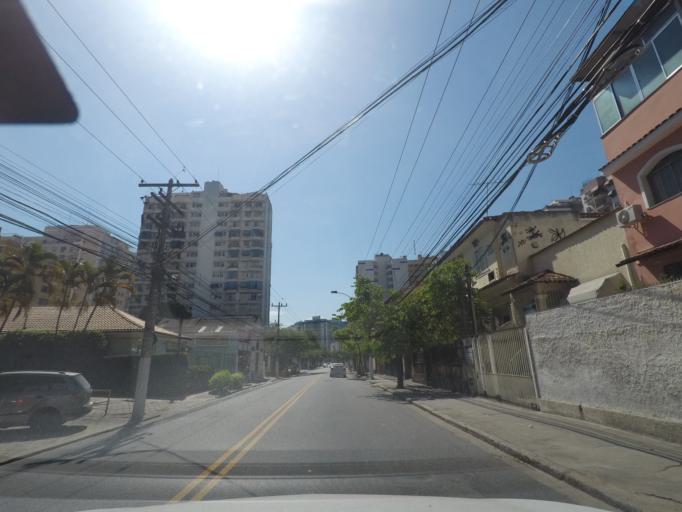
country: BR
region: Rio de Janeiro
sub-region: Niteroi
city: Niteroi
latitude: -22.9037
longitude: -43.0945
